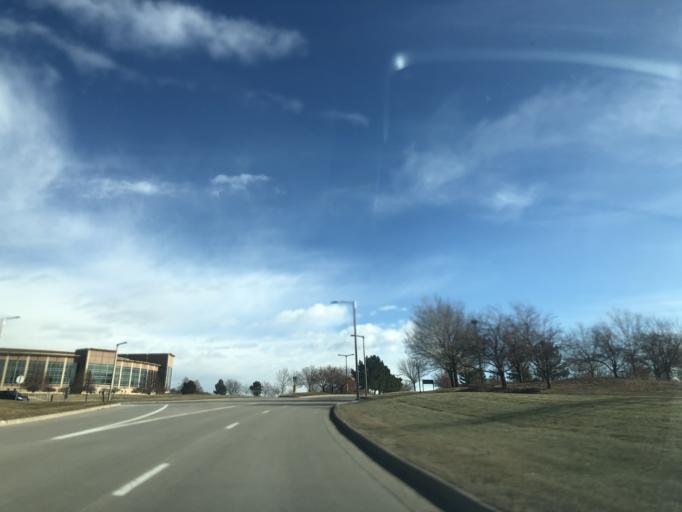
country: US
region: Colorado
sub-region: Douglas County
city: Meridian
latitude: 39.5480
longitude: -104.8457
